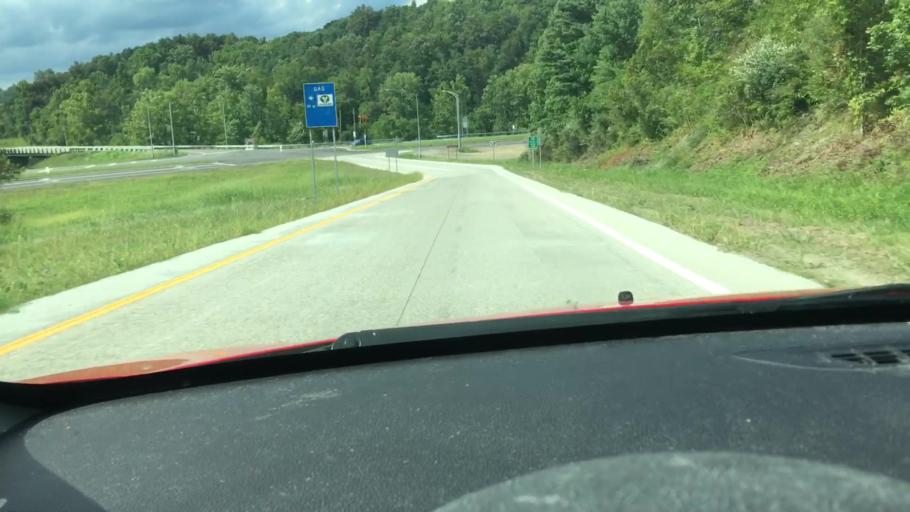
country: US
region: Ohio
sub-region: Athens County
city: The Plains
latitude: 39.3610
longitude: -82.1049
